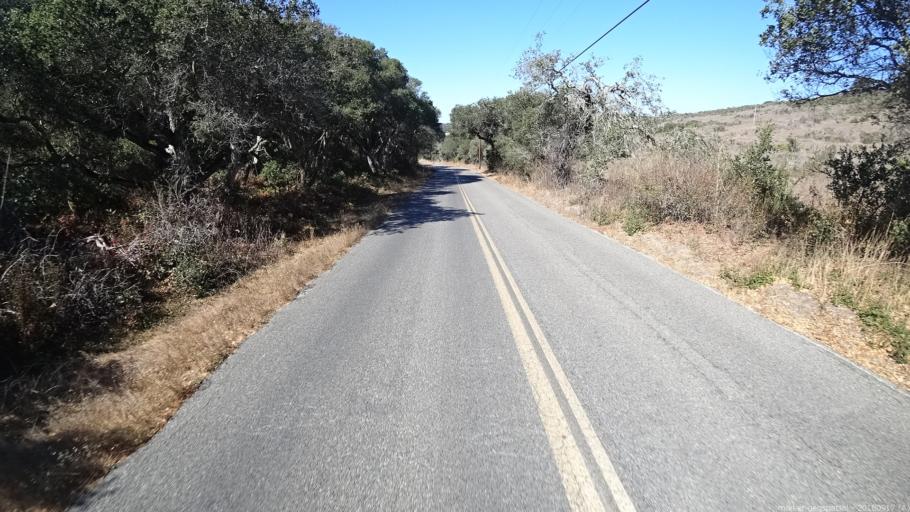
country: US
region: California
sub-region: Monterey County
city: Elkhorn
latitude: 36.8327
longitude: -121.6887
